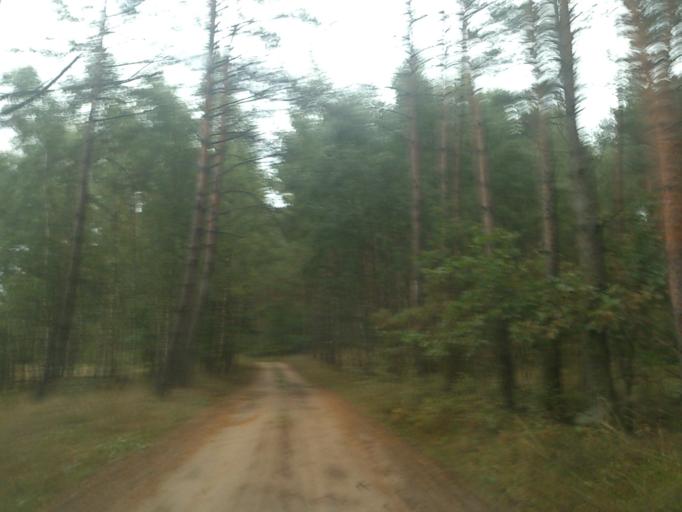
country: PL
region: Kujawsko-Pomorskie
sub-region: Powiat golubsko-dobrzynski
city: Golub-Dobrzyn
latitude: 53.1179
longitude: 19.0937
